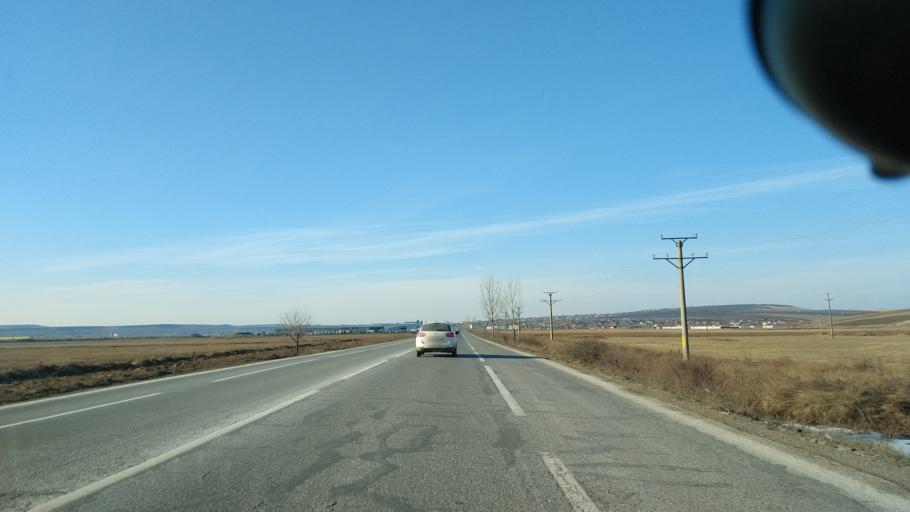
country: RO
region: Iasi
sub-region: Comuna Letcani
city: Letcani
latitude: 47.1868
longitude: 27.4454
